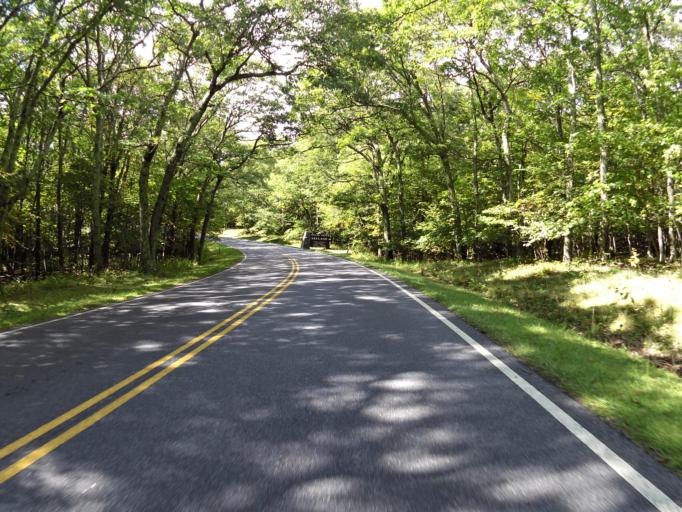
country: US
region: Virginia
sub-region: Page County
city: Luray
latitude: 38.5923
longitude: -78.3730
